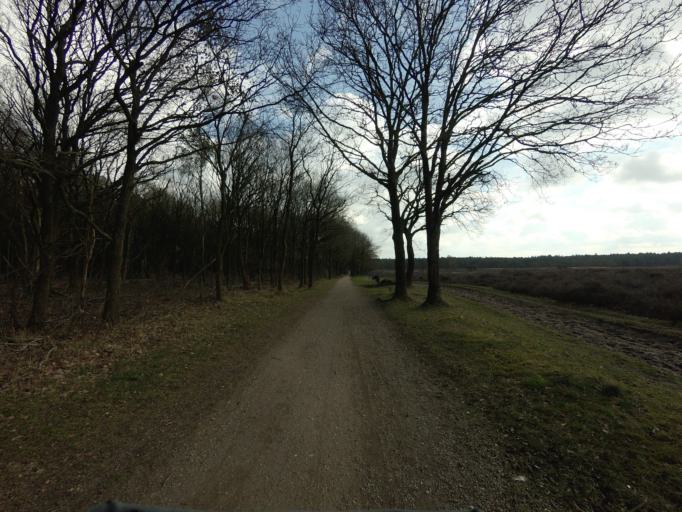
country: NL
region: North Holland
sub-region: Gemeente Hilversum
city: Hilversum
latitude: 52.2032
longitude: 5.1699
